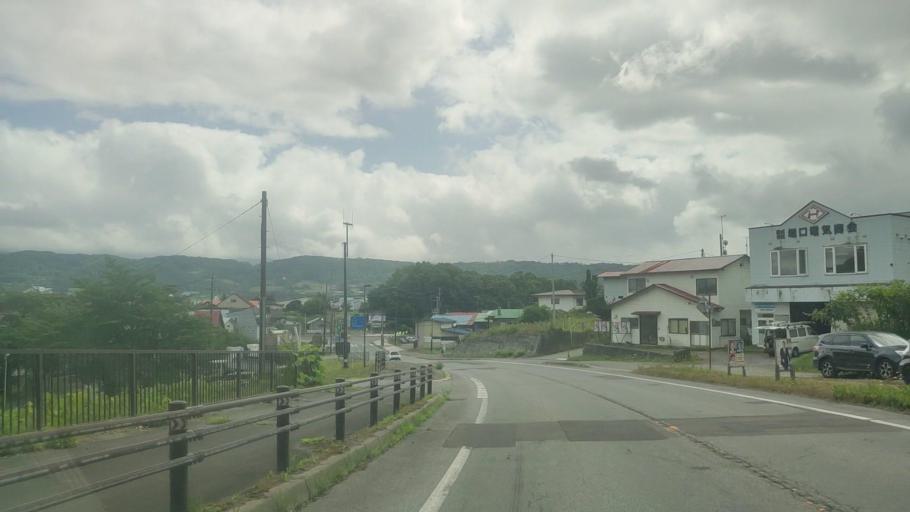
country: JP
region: Hokkaido
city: Date
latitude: 42.5587
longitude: 140.8864
